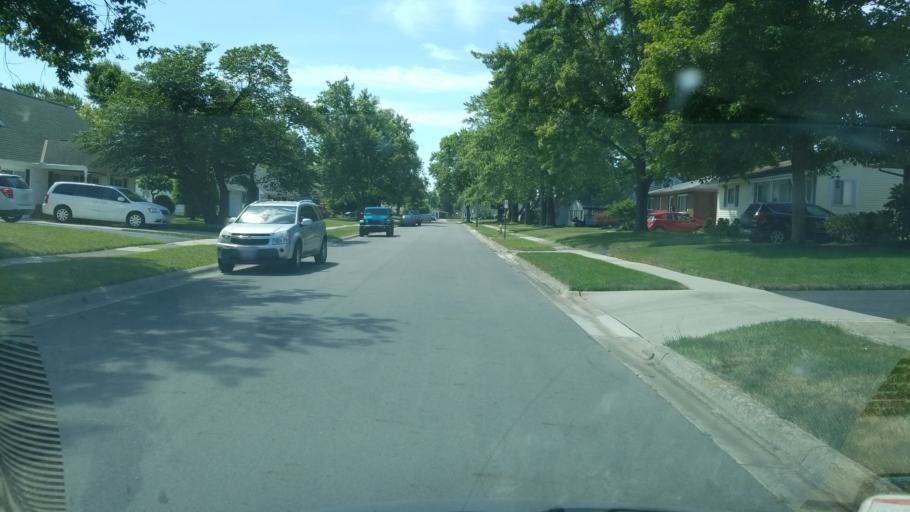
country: US
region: Ohio
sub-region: Franklin County
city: Grove City
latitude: 39.8761
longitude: -83.0798
